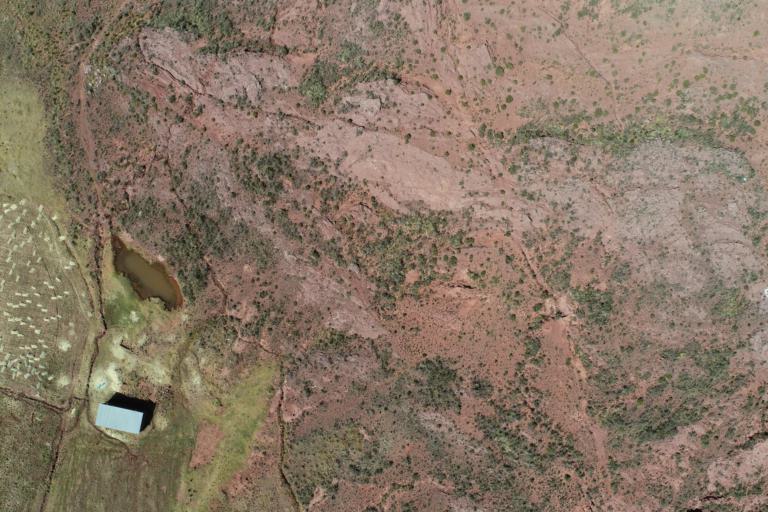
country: BO
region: La Paz
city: Tiahuanaco
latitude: -16.5968
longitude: -68.7565
